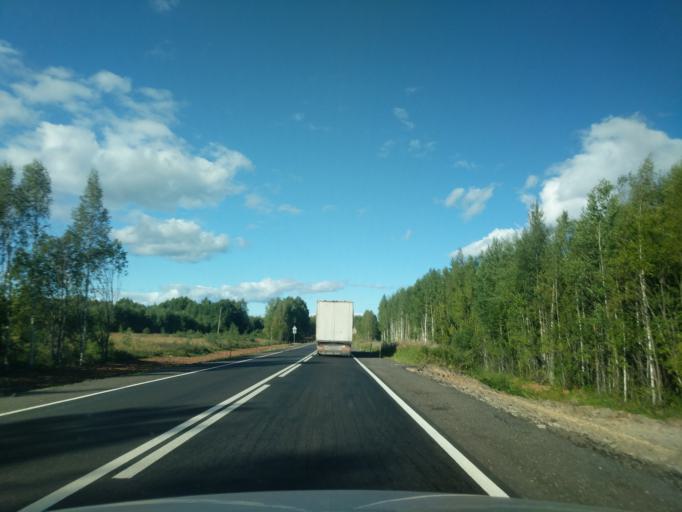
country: RU
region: Kostroma
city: Makar'yev
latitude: 57.9899
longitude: 43.9663
